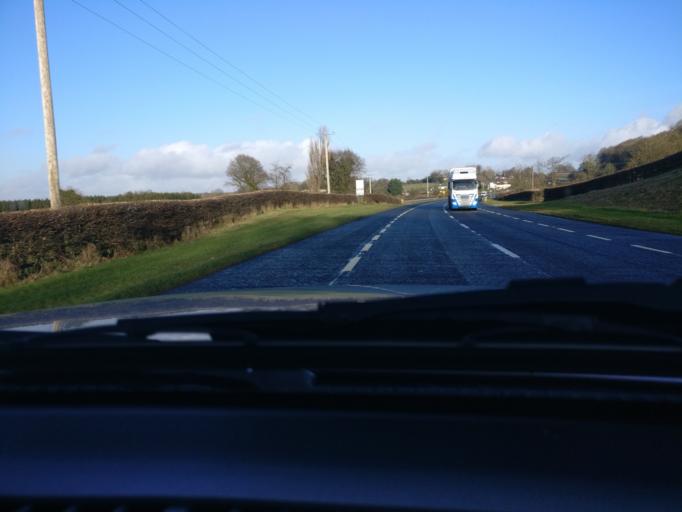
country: IE
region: Leinster
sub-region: An Iarmhi
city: An Muileann gCearr
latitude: 53.5418
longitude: -7.3002
